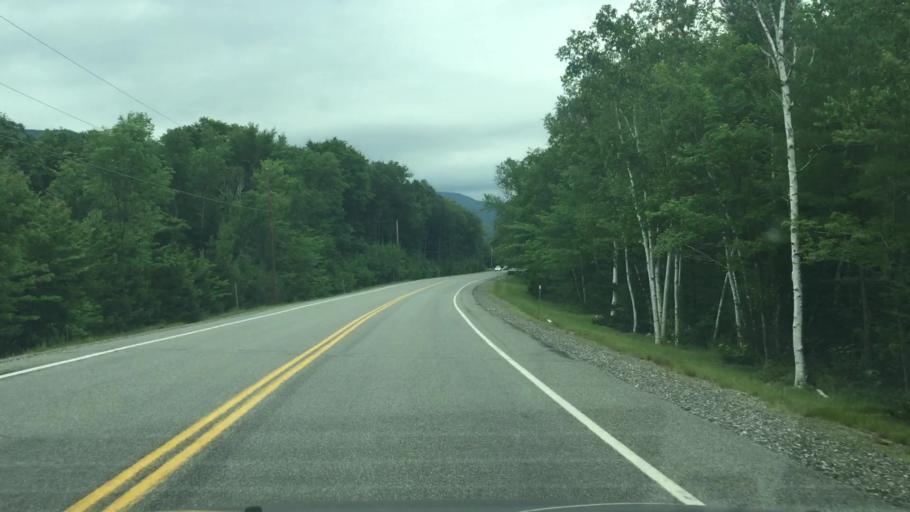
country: US
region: New Hampshire
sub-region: Carroll County
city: North Conway
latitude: 44.1305
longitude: -71.3603
